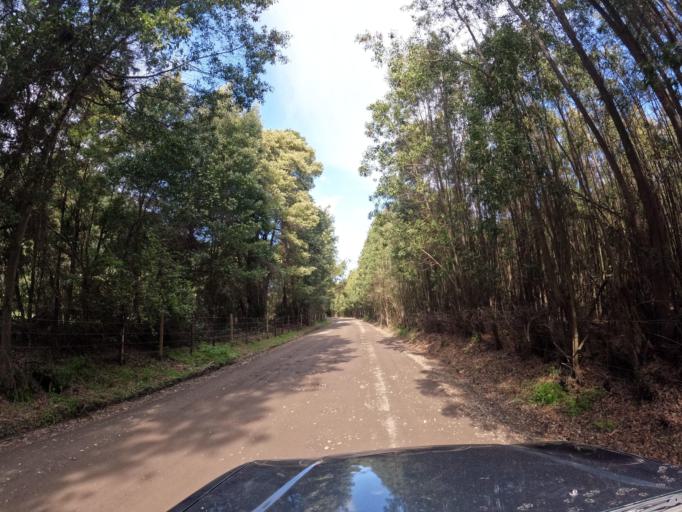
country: CL
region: Biobio
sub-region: Provincia de Concepcion
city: Chiguayante
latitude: -37.0495
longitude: -72.9583
